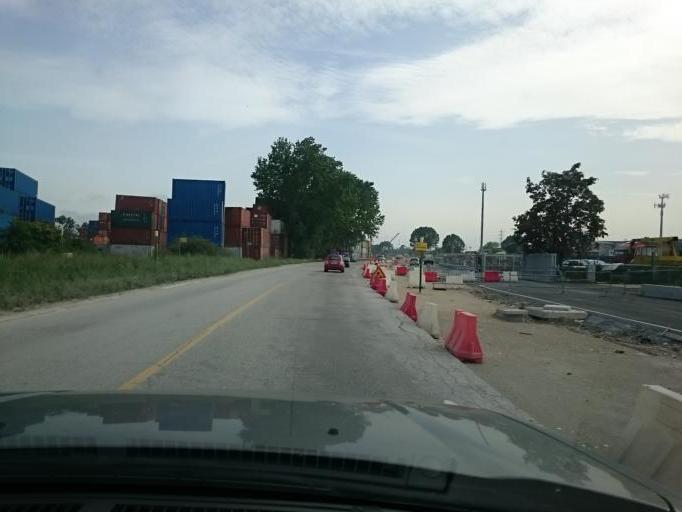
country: IT
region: Veneto
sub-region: Provincia di Venezia
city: Mestre
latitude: 45.4476
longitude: 12.2126
